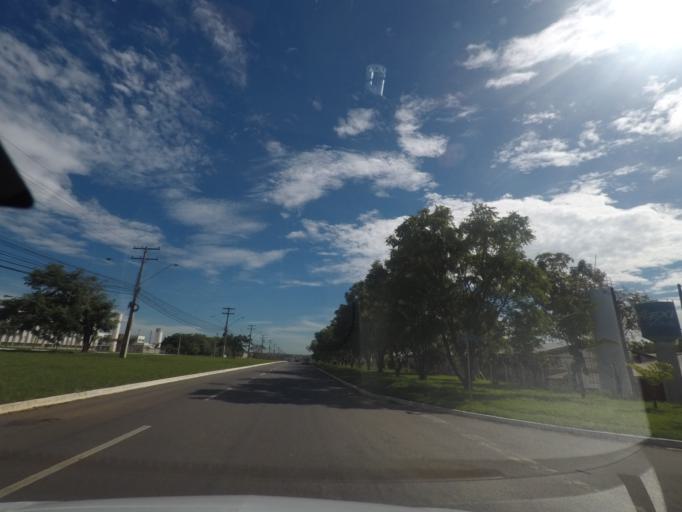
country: BR
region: Goias
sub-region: Aparecida De Goiania
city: Aparecida de Goiania
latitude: -16.7959
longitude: -49.2545
